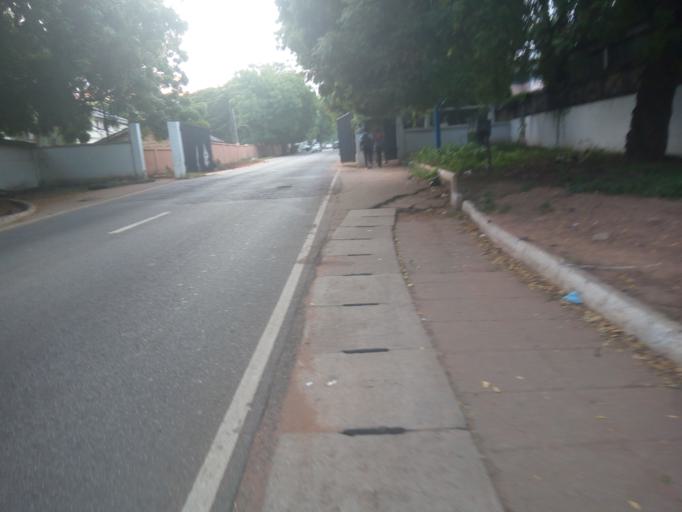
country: GH
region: Greater Accra
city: Accra
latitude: 5.5559
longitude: -0.1932
